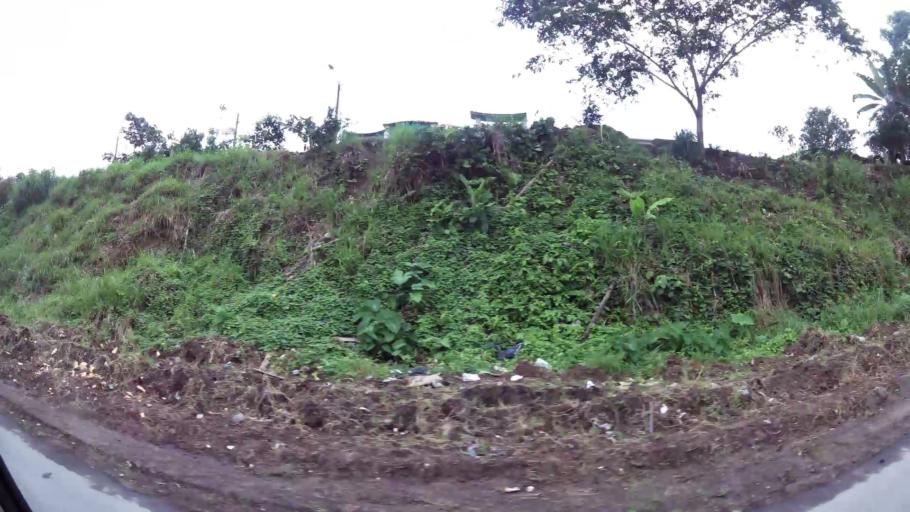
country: EC
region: Santo Domingo de los Tsachilas
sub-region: Canton Santo Domingo de los Colorados
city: Santo Domingo de los Colorados
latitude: -0.2683
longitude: -79.1442
